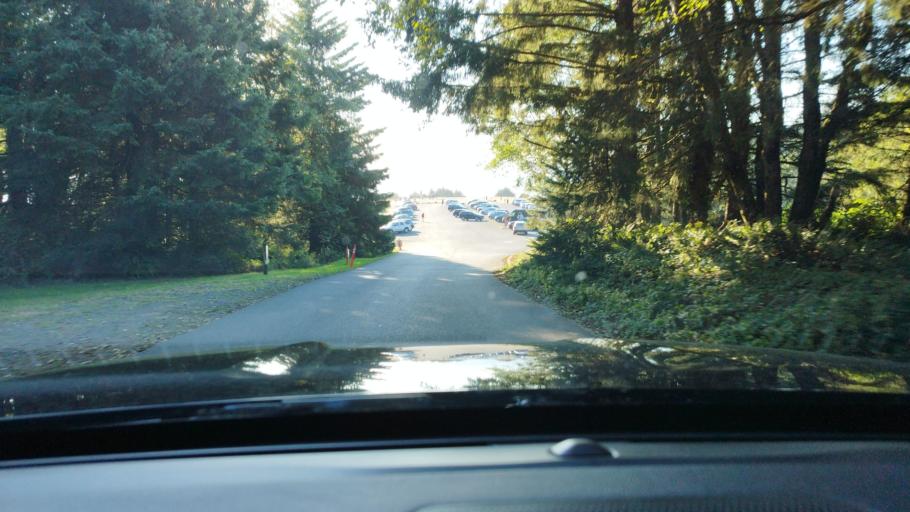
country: US
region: Oregon
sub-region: Clatsop County
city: Cannon Beach
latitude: 45.9193
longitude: -123.9715
